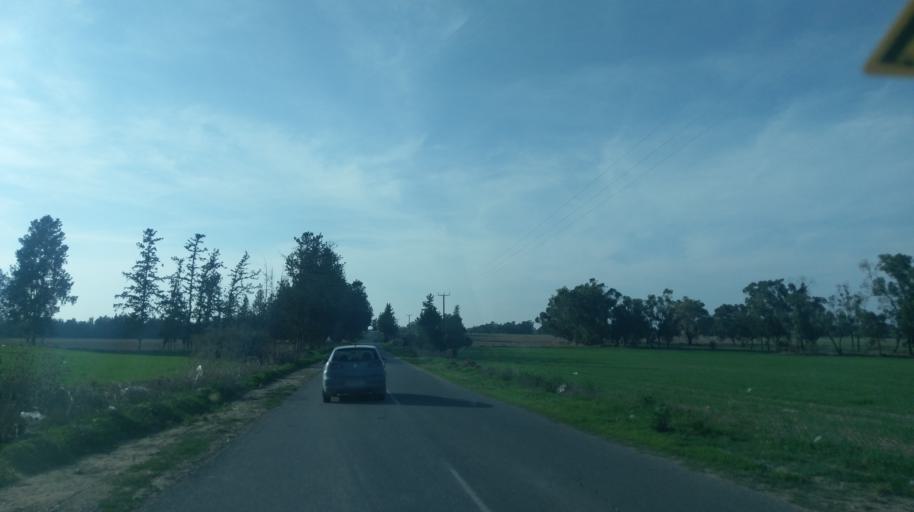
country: CY
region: Ammochostos
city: Achna
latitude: 35.1097
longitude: 33.7415
